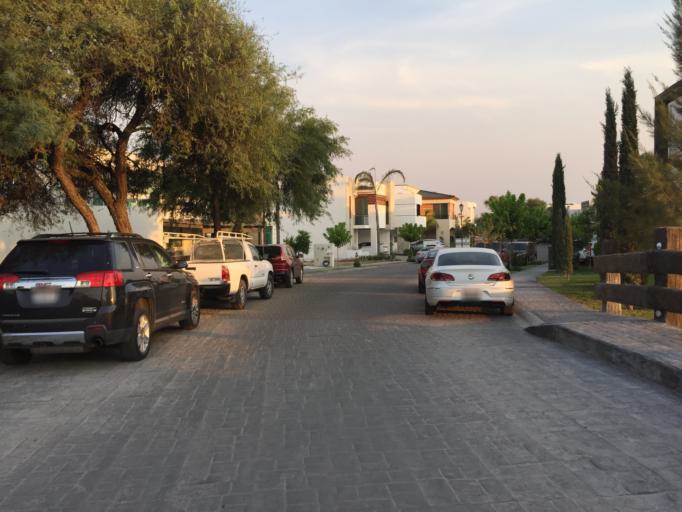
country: MX
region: Aguascalientes
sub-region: Aguascalientes
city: La Loma de los Negritos
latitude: 21.8472
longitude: -102.3565
